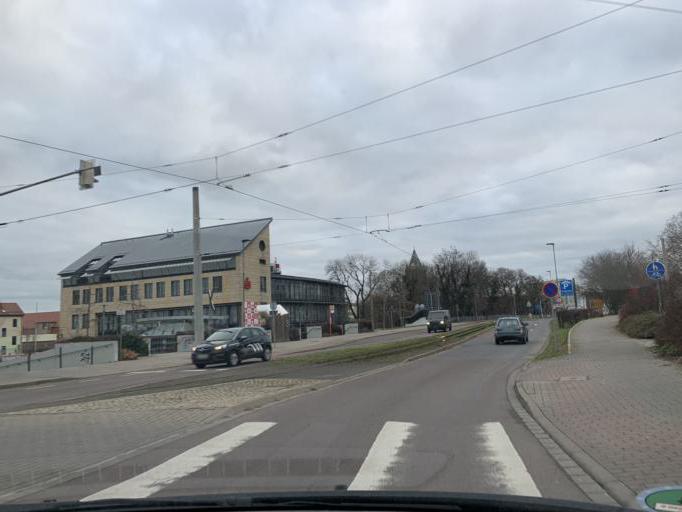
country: DE
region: Saxony-Anhalt
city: Merseburg
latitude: 51.3543
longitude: 11.9928
